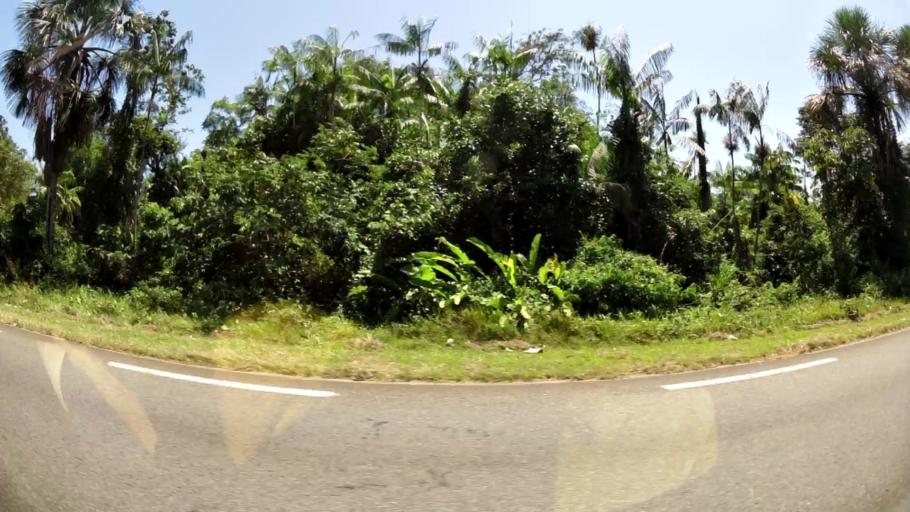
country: GF
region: Guyane
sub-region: Guyane
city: Cayenne
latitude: 4.9126
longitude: -52.3278
